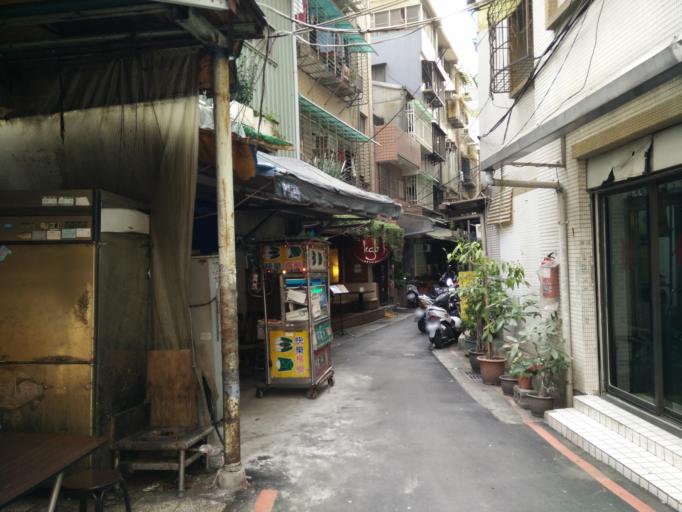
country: TW
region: Taipei
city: Taipei
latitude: 25.0219
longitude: 121.5282
